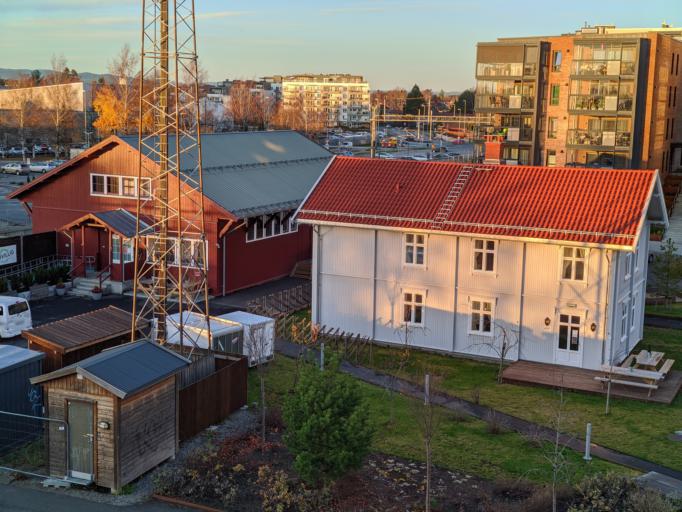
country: NO
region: Akershus
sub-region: Ullensaker
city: Jessheim
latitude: 60.1416
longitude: 11.1777
